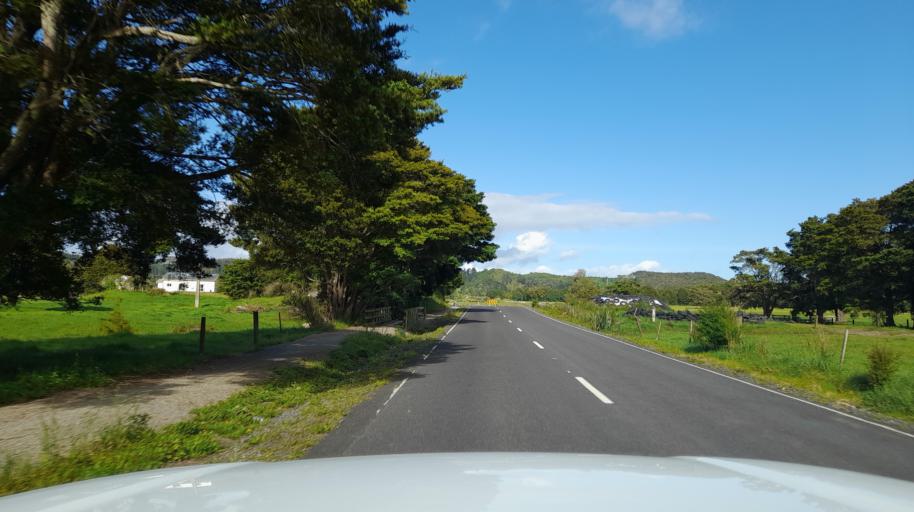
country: NZ
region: Northland
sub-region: Far North District
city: Moerewa
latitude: -35.4036
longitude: 173.9813
